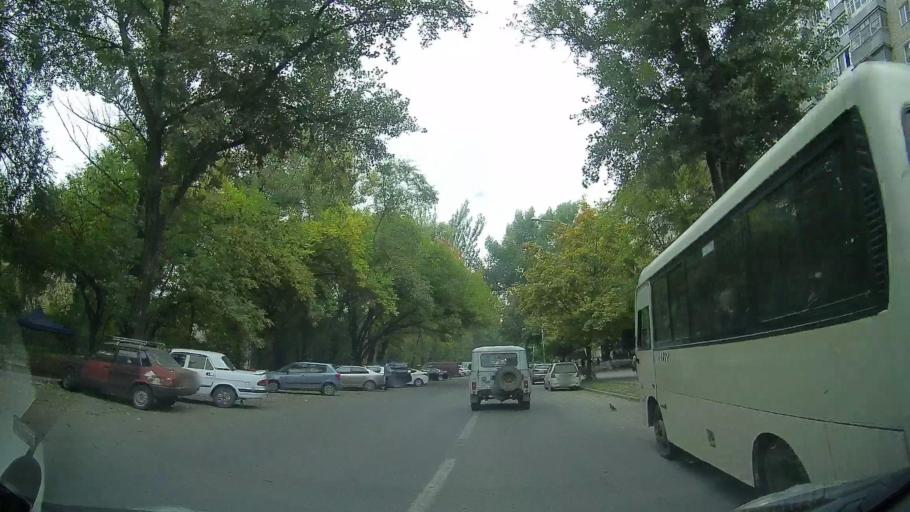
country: RU
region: Rostov
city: Severnyy
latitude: 47.2672
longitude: 39.6657
